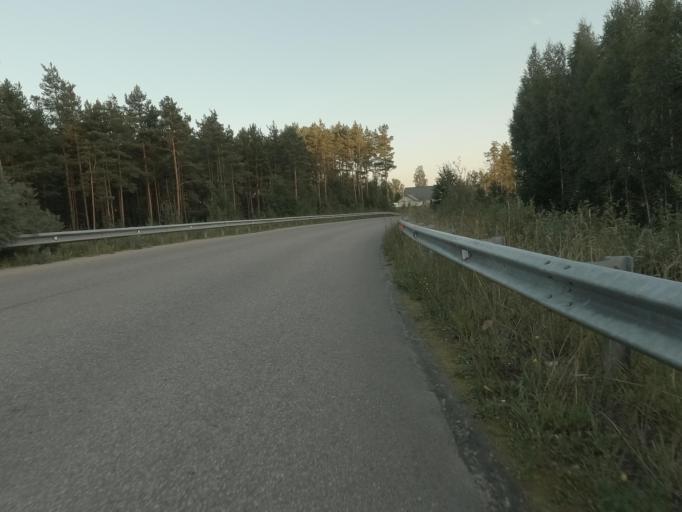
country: RU
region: Leningrad
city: Mga
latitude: 59.7617
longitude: 31.0403
